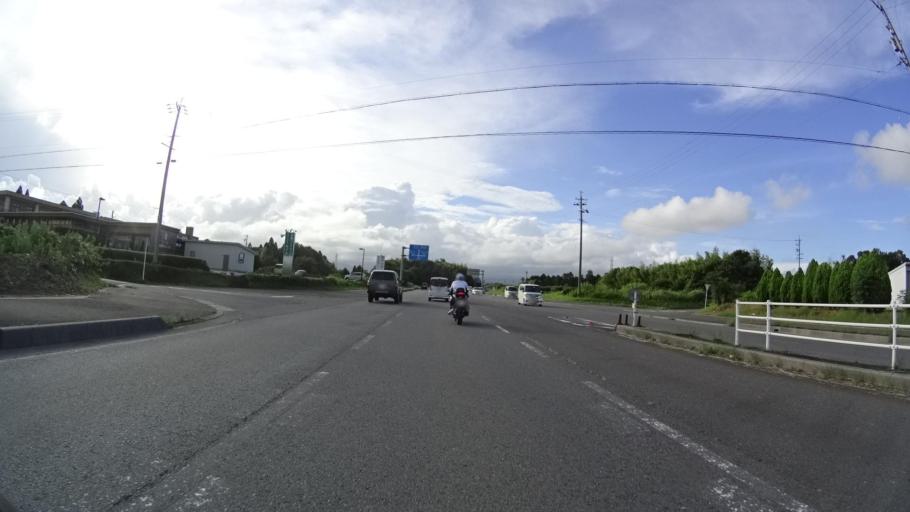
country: JP
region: Mie
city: Kameyama
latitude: 34.8878
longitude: 136.5099
